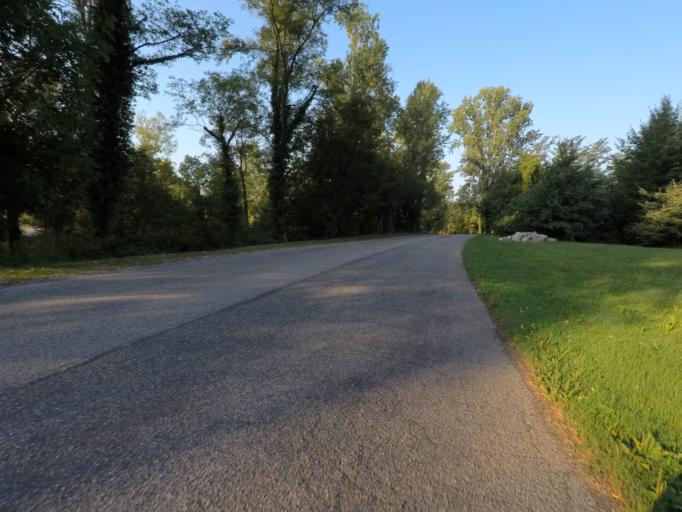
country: IT
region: Friuli Venezia Giulia
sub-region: Provincia di Udine
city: Trasaghis
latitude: 46.2801
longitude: 13.0812
